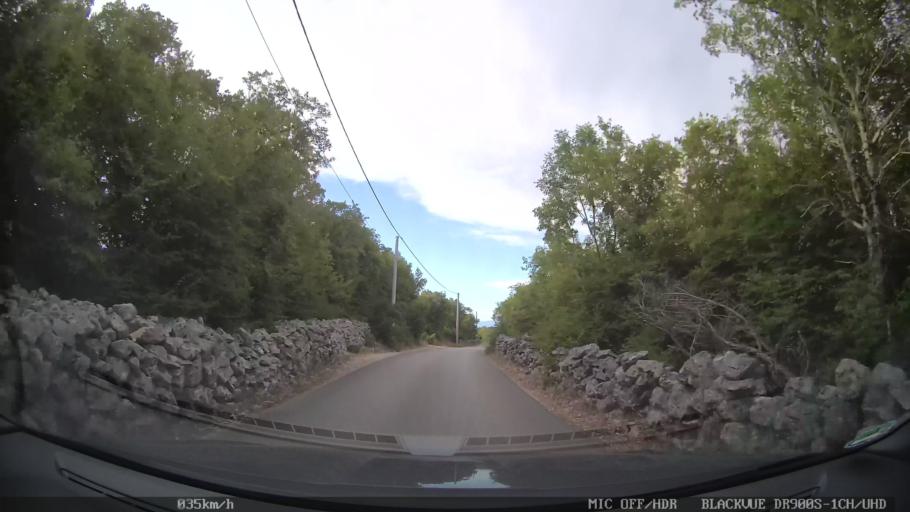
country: HR
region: Primorsko-Goranska
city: Njivice
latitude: 45.0836
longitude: 14.4429
